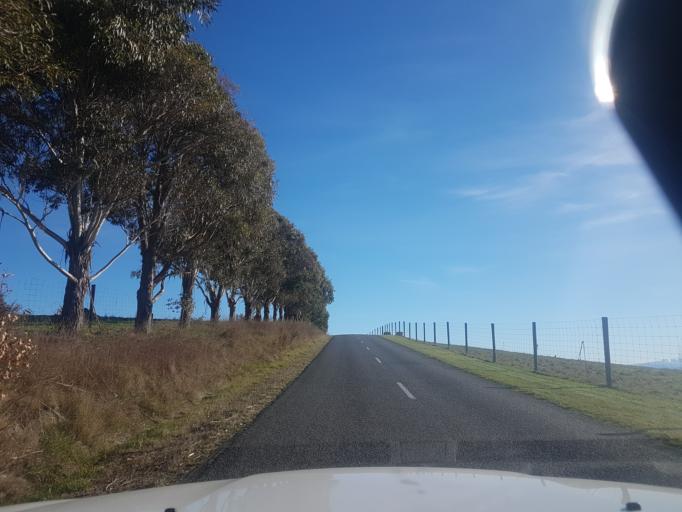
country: NZ
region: Canterbury
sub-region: Timaru District
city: Pleasant Point
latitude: -44.2476
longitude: 171.0813
